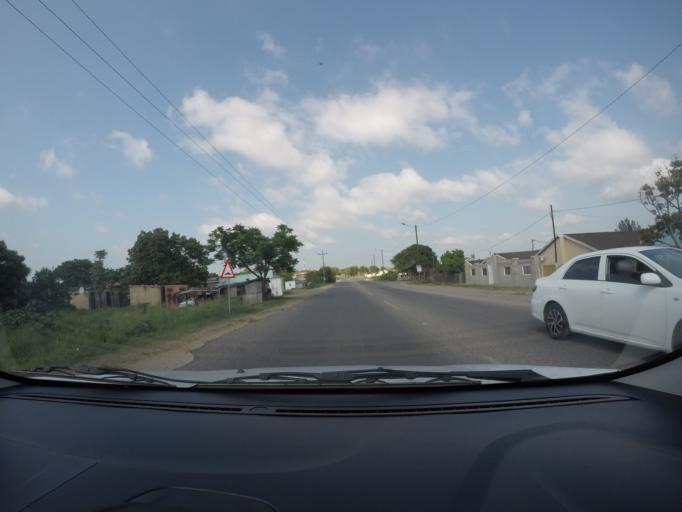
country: ZA
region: KwaZulu-Natal
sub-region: uThungulu District Municipality
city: eSikhawini
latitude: -28.8718
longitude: 31.9219
